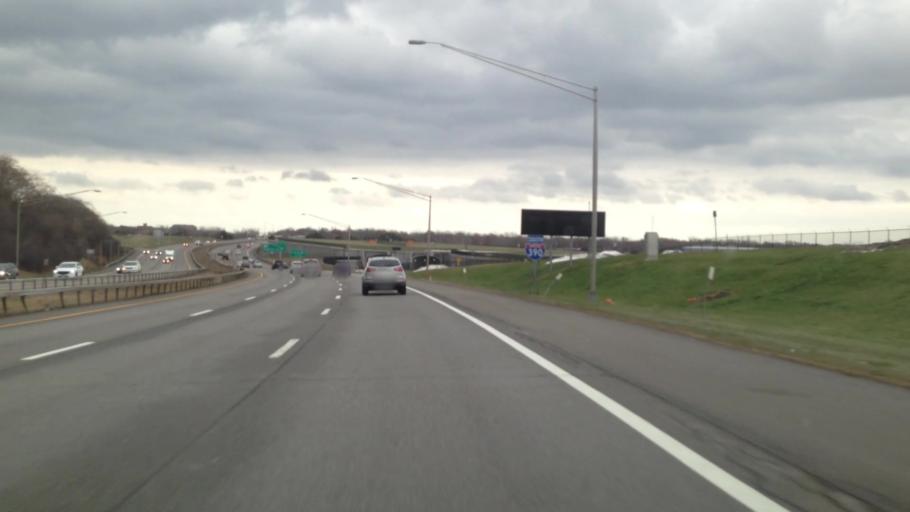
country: US
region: New York
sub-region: Monroe County
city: Rochester
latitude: 43.1261
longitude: -77.6568
